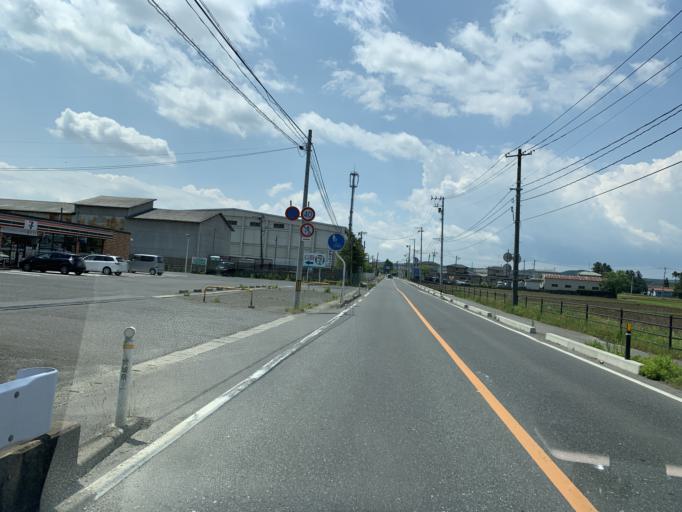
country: JP
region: Miyagi
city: Kogota
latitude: 38.5363
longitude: 141.0550
